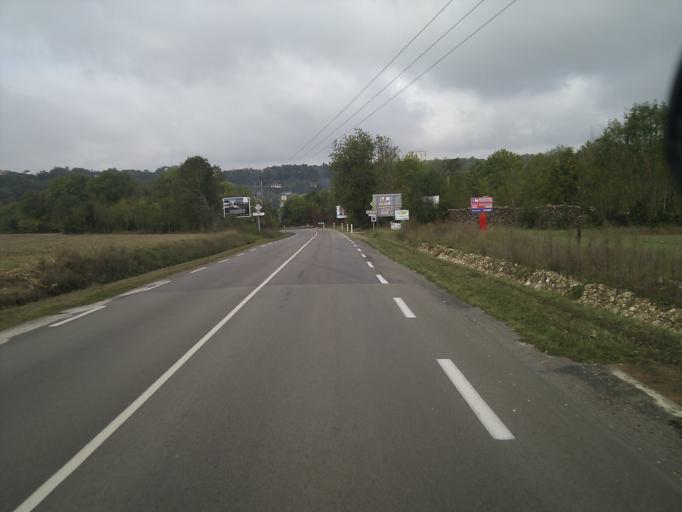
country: FR
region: Champagne-Ardenne
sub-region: Departement de la Haute-Marne
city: Chaumont
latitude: 48.1179
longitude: 5.1588
